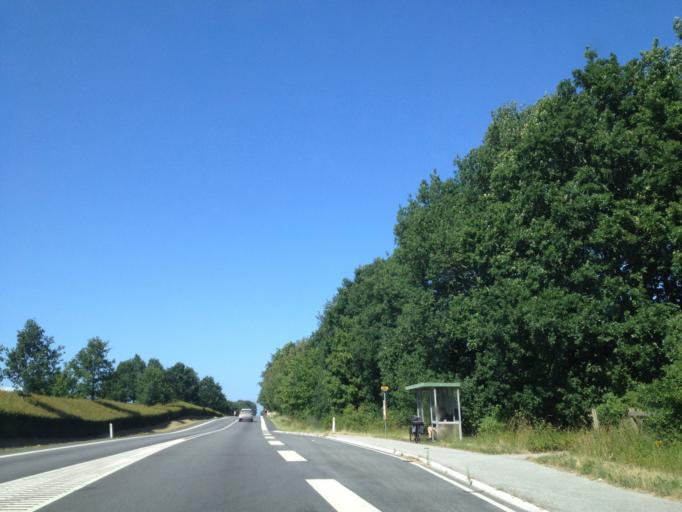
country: DK
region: Capital Region
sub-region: Fredensborg Kommune
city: Niva
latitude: 55.9621
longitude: 12.4950
